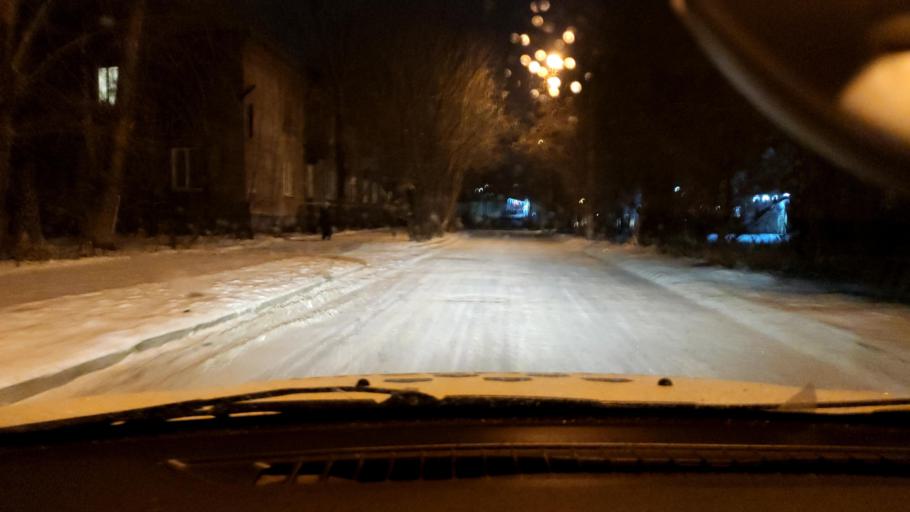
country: RU
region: Perm
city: Overyata
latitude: 58.0016
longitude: 55.9309
